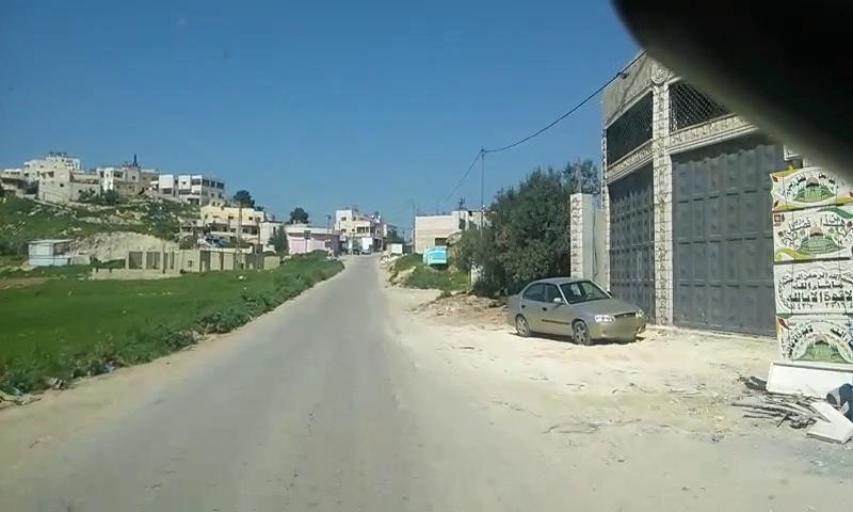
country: PS
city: Dayr Samit
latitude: 31.5165
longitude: 34.9710
